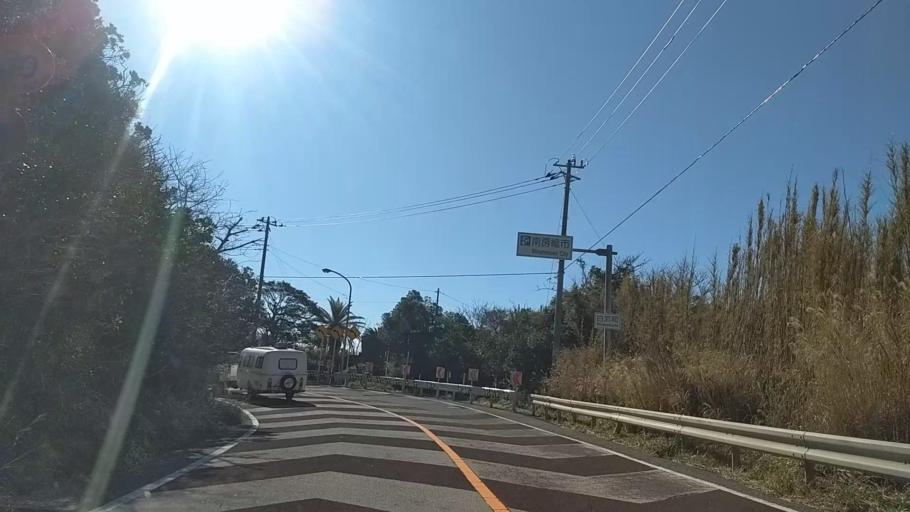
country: JP
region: Chiba
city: Tateyama
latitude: 34.9120
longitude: 139.8258
